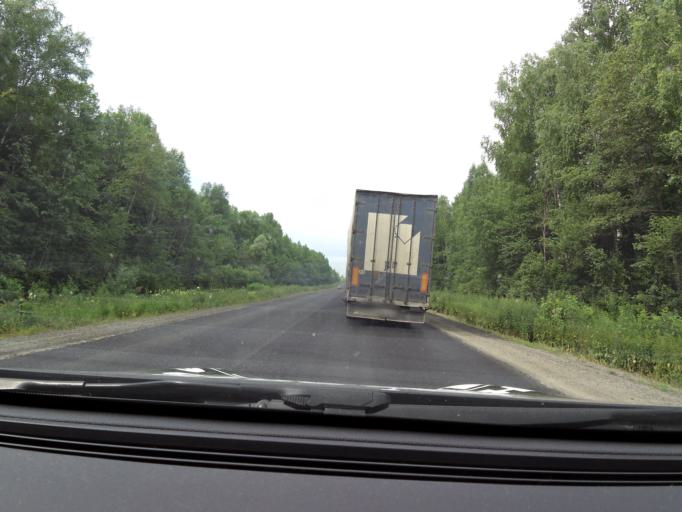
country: RU
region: Chelyabinsk
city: Asha
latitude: 54.8679
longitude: 57.1756
